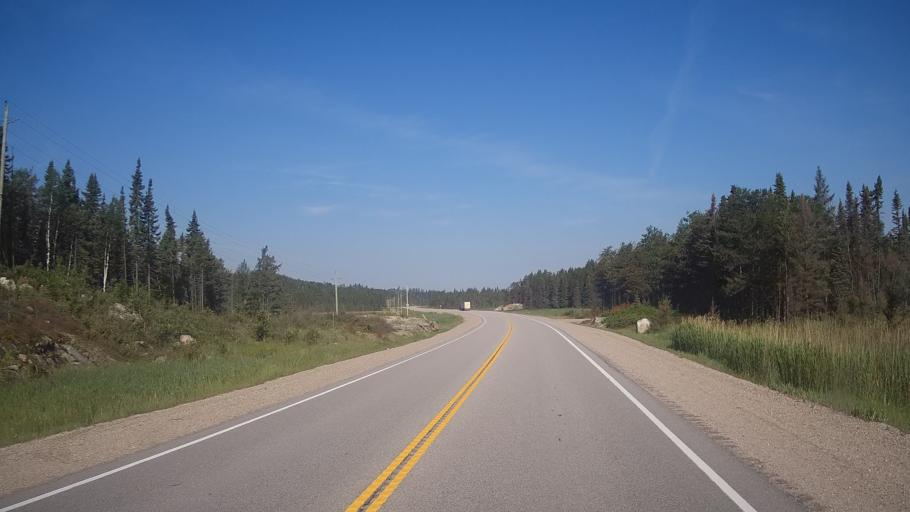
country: CA
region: Ontario
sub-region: Rainy River District
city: Atikokan
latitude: 49.4586
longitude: -91.8586
